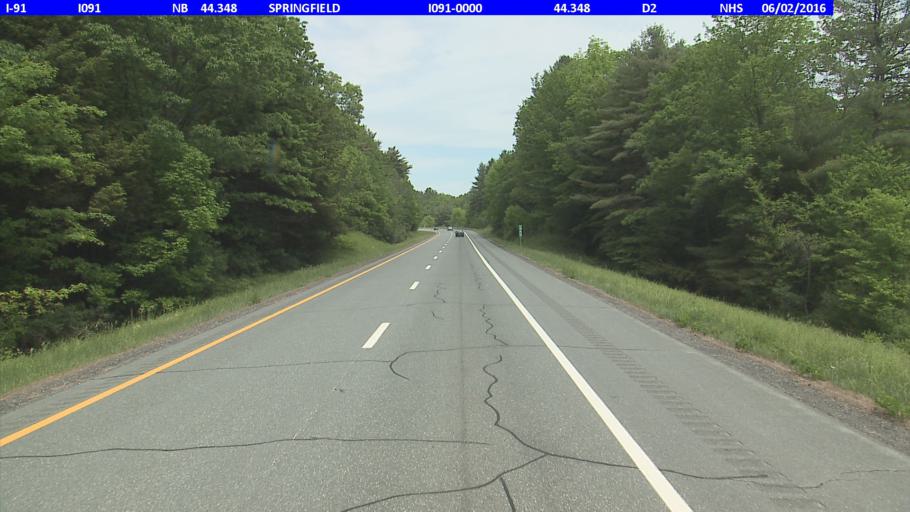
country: US
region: Vermont
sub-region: Windsor County
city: Springfield
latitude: 43.3035
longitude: -72.4238
